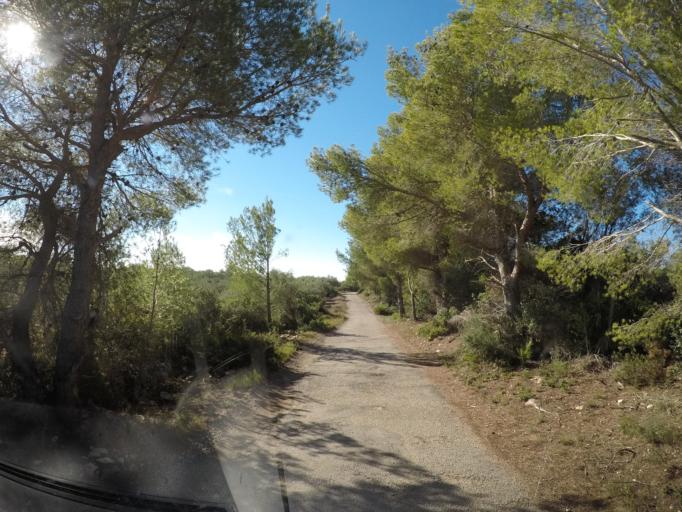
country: ES
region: Catalonia
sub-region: Provincia de Tarragona
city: El Perello
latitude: 40.9144
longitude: 0.7233
